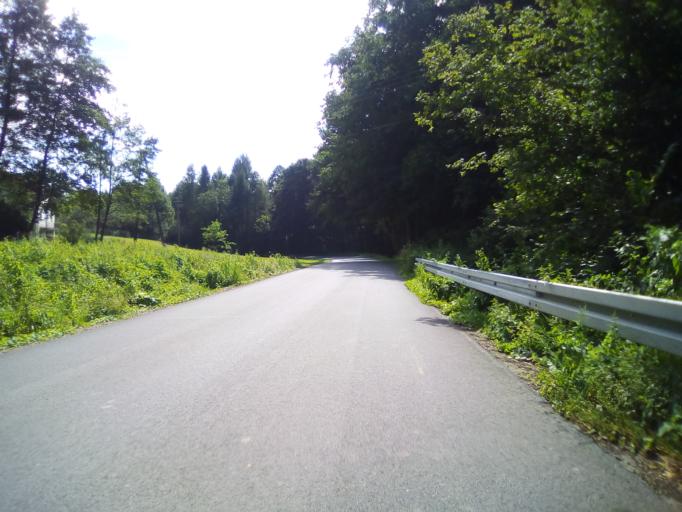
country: PL
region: Subcarpathian Voivodeship
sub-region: Powiat strzyzowski
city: Konieczkowa
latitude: 49.8155
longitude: 21.9236
